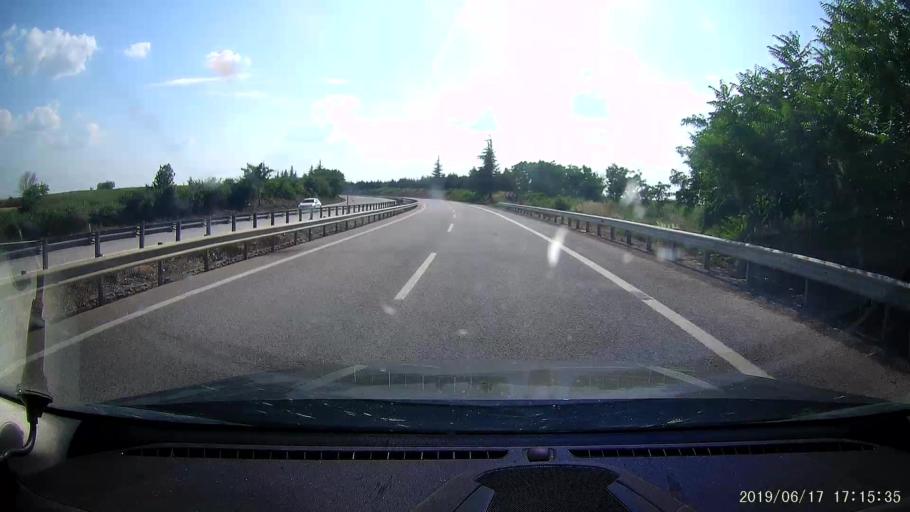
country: GR
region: East Macedonia and Thrace
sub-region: Nomos Evrou
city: Kastanies
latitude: 41.7021
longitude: 26.4931
